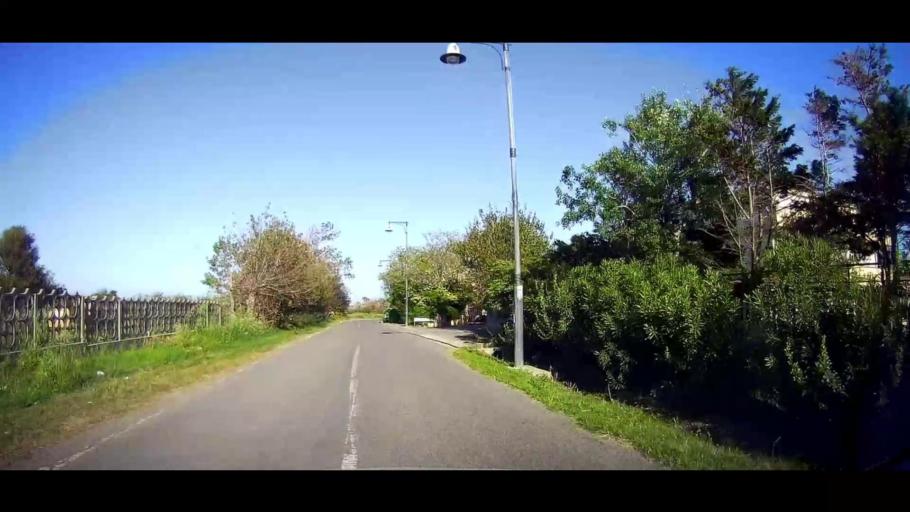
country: IT
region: Calabria
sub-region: Provincia di Crotone
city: Crotone
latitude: 39.0256
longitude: 17.1944
